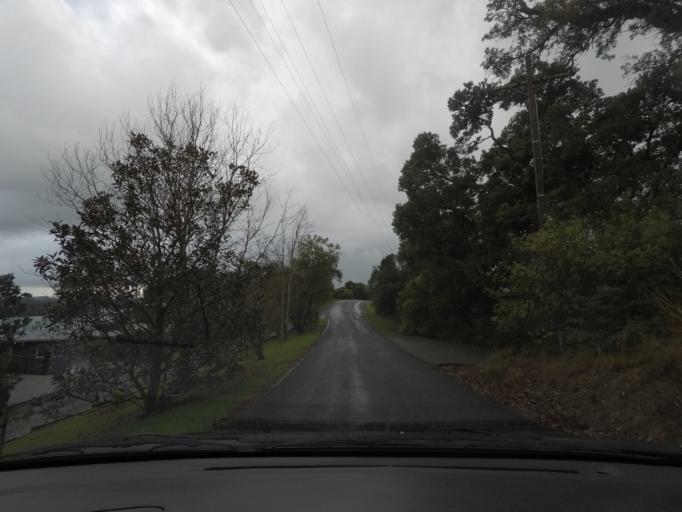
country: NZ
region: Auckland
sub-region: Auckland
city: Warkworth
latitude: -36.4808
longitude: 174.7289
